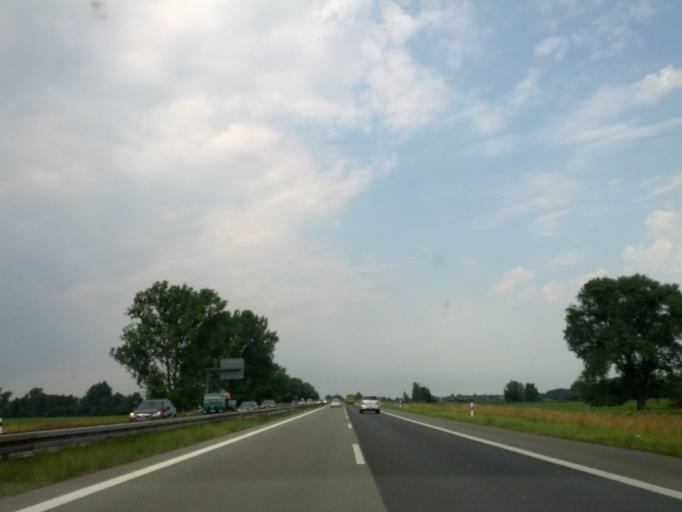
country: DE
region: Brandenburg
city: Fehrbellin
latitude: 52.8166
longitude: 12.7943
